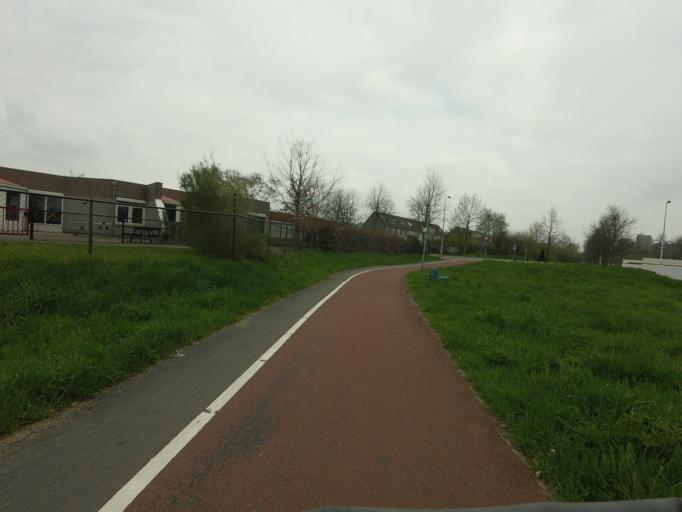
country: NL
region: Utrecht
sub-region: Gemeente Utrecht
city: Utrecht
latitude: 52.1209
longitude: 5.0929
